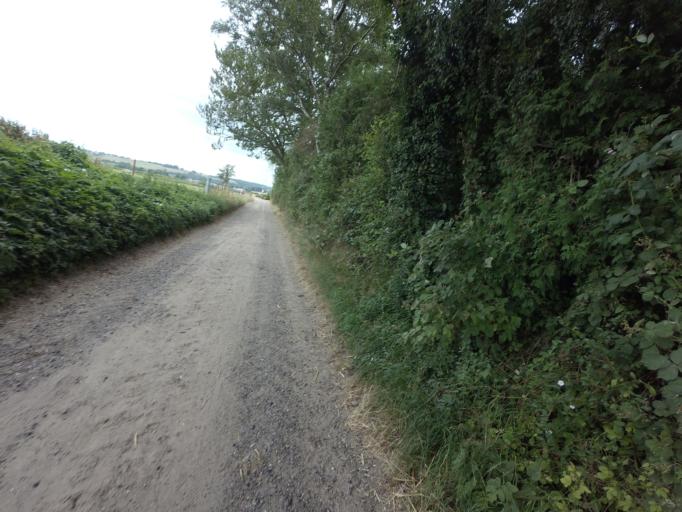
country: NL
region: Limburg
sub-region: Gemeente Voerendaal
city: Ubachsberg
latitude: 50.8045
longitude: 5.9347
